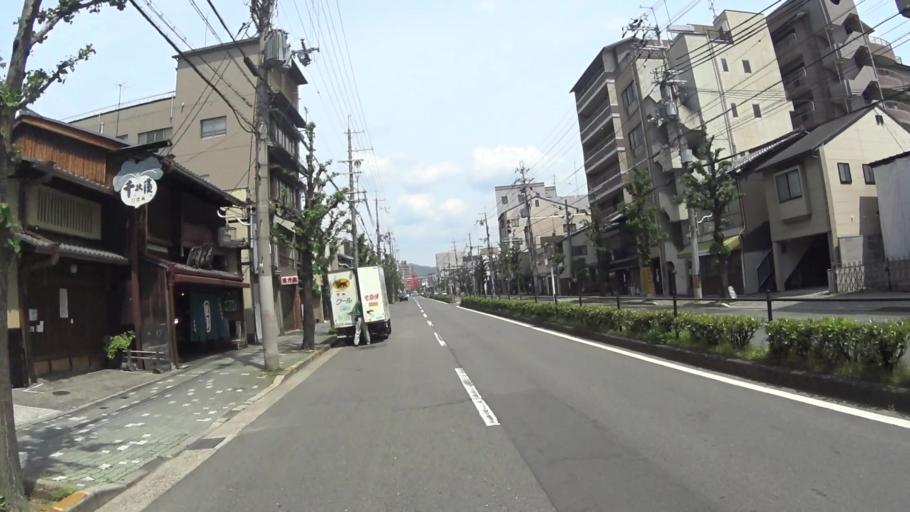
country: JP
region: Kyoto
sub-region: Kyoto-shi
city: Kamigyo-ku
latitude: 35.0312
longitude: 135.7422
